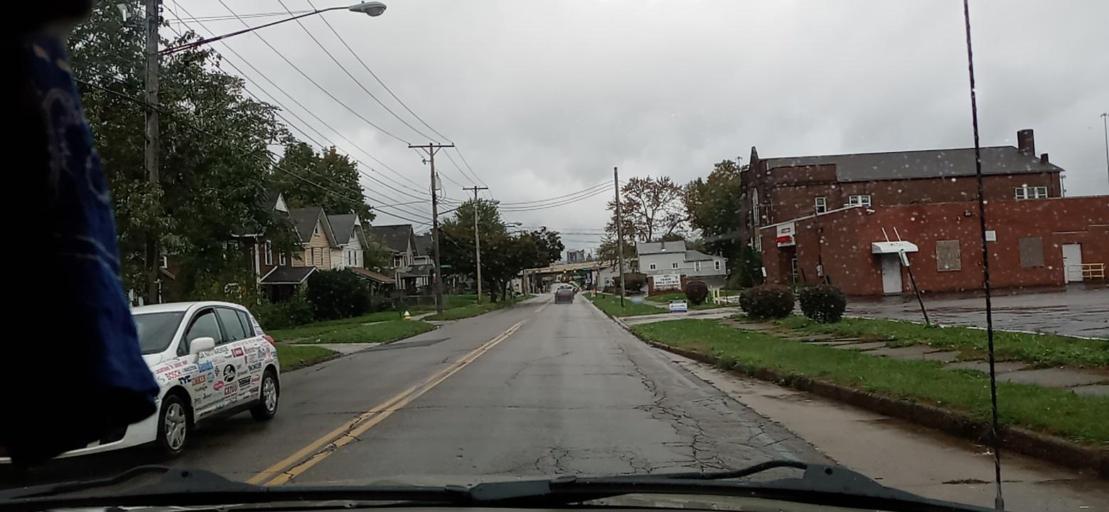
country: US
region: Ohio
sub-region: Summit County
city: Akron
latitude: 41.0599
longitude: -81.5098
